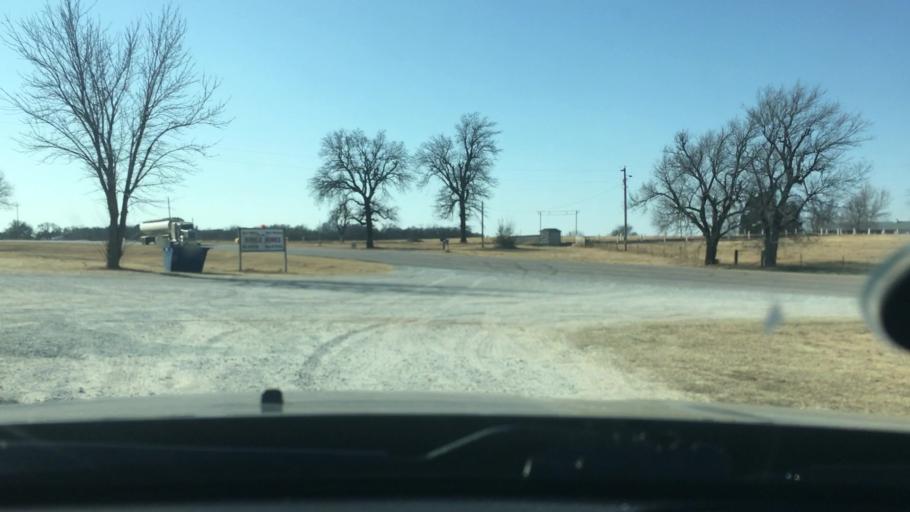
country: US
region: Oklahoma
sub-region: Garvin County
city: Stratford
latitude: 34.8519
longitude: -96.9670
